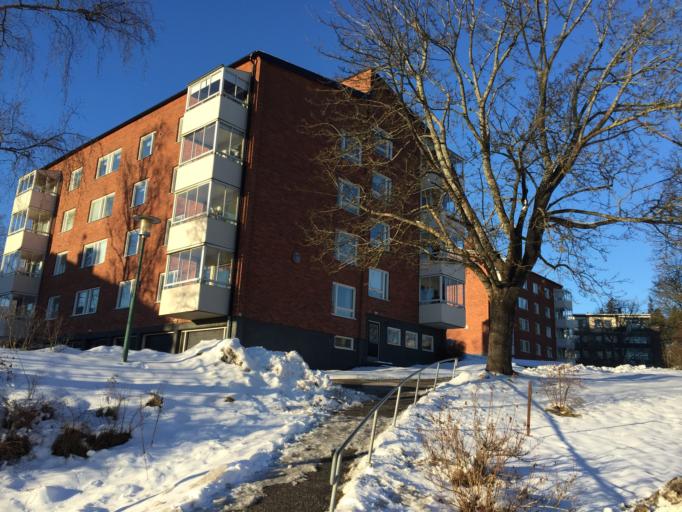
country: SE
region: Stockholm
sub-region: Salems Kommun
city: Ronninge
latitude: 59.1947
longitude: 17.7493
